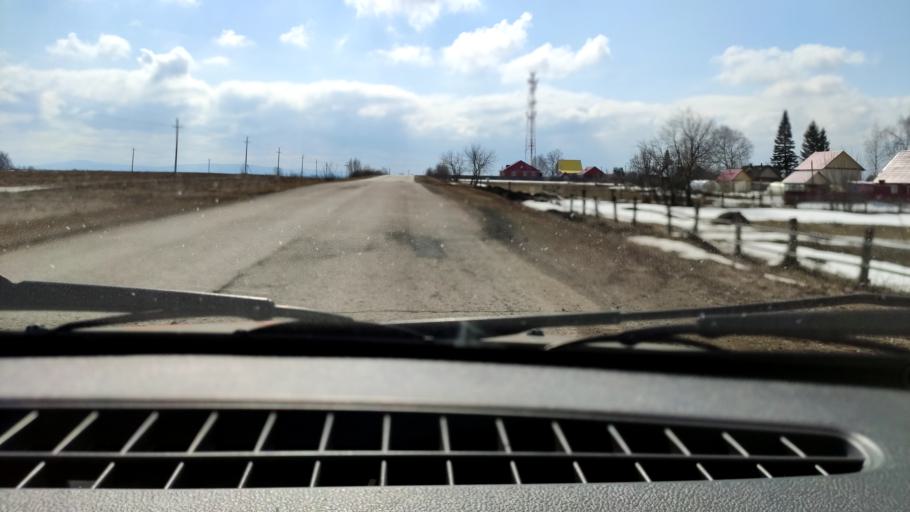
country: RU
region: Bashkortostan
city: Kudeyevskiy
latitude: 54.8473
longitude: 56.7956
